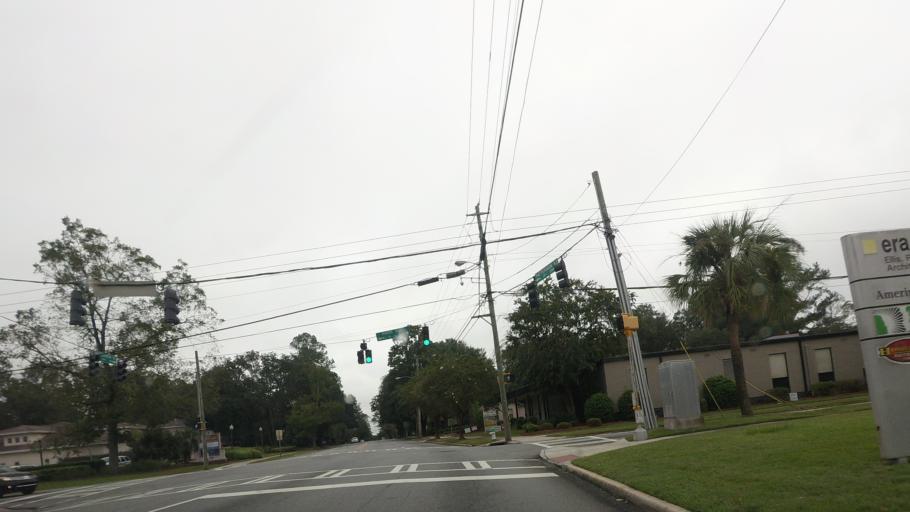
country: US
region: Georgia
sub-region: Lowndes County
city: Remerton
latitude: 30.8567
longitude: -83.2891
